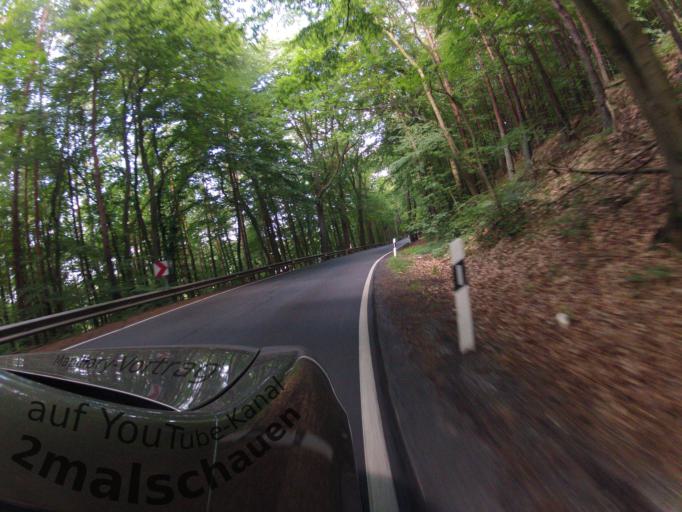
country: DE
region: Mecklenburg-Vorpommern
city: Seebad Heringsdorf
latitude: 53.9315
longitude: 14.1863
